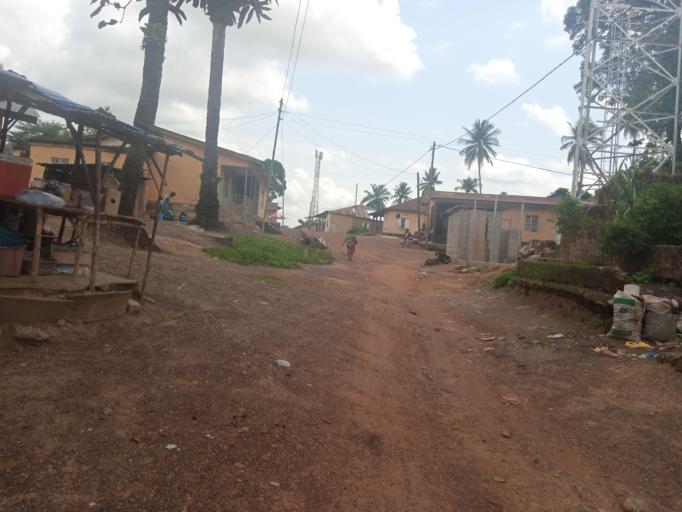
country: SL
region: Southern Province
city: Bo
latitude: 7.9559
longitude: -11.7391
